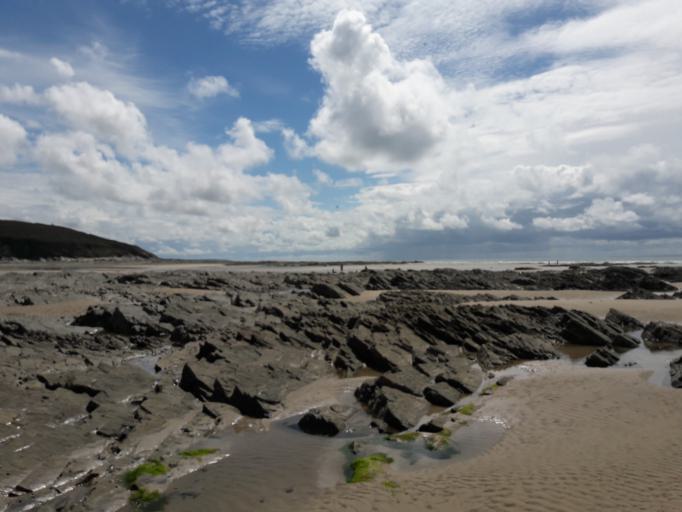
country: FR
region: Lower Normandy
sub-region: Departement de la Manche
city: Surtainville
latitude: 49.4803
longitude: -1.8505
